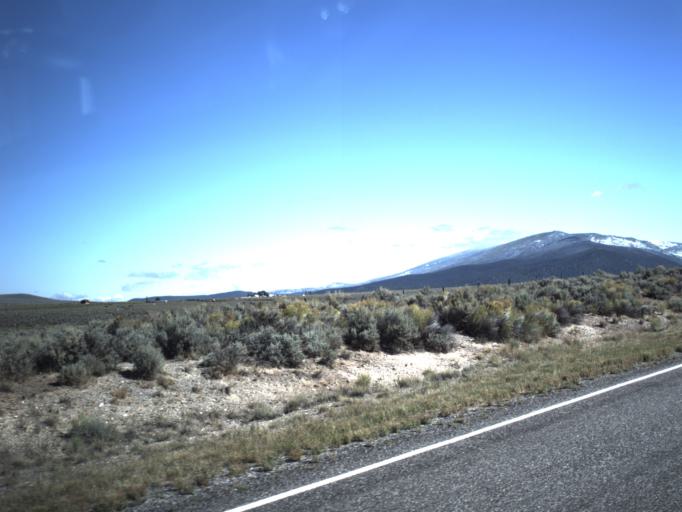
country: US
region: Utah
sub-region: Wayne County
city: Loa
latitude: 38.5659
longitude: -111.8452
